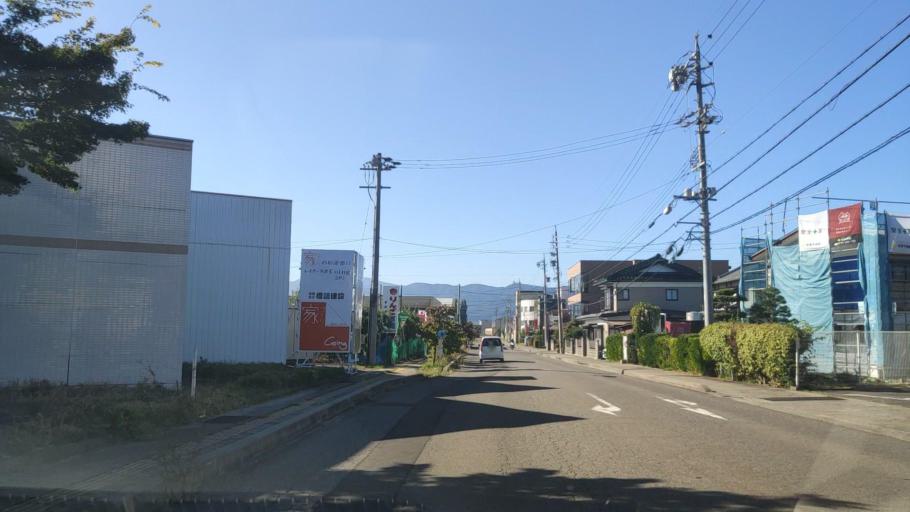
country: JP
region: Nagano
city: Okaya
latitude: 36.0659
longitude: 138.0802
